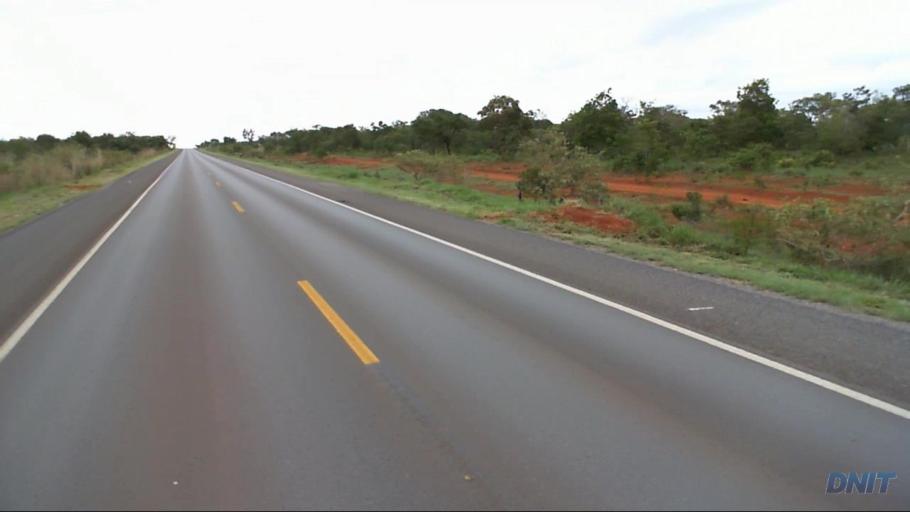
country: BR
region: Goias
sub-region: Barro Alto
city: Barro Alto
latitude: -15.2093
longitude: -48.6789
